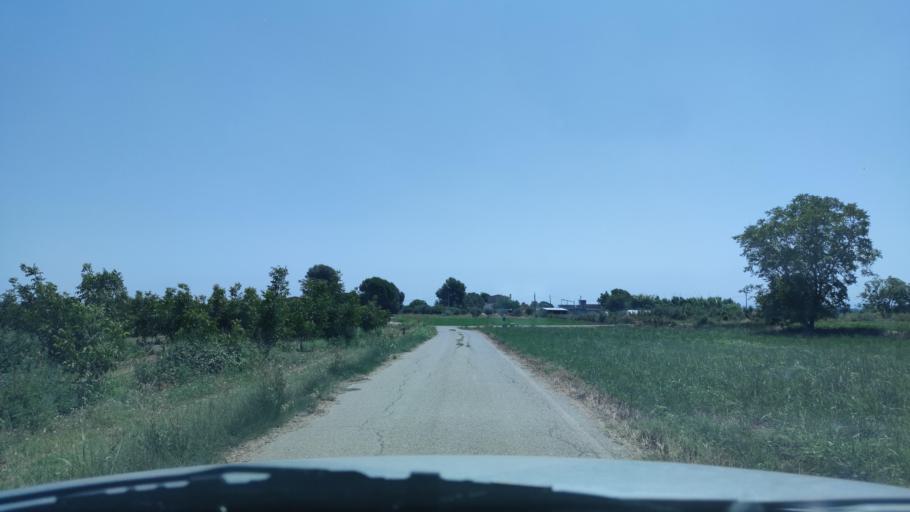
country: ES
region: Catalonia
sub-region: Provincia de Lleida
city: Torrefarrera
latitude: 41.6480
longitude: 0.5875
